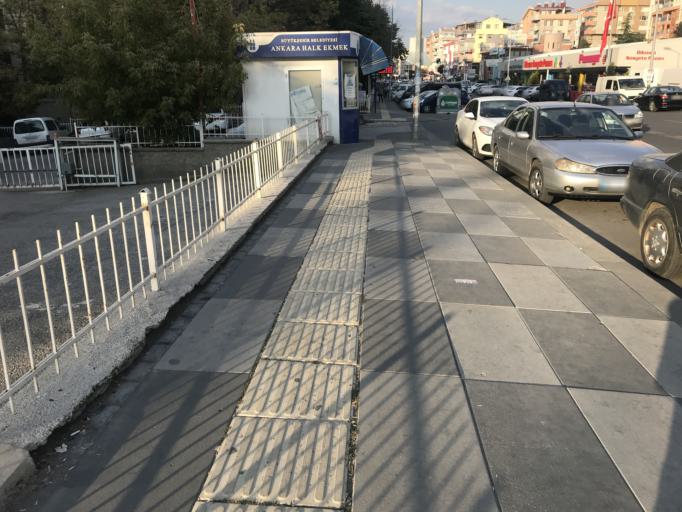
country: TR
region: Ankara
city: Ankara
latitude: 39.8691
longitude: 32.8251
